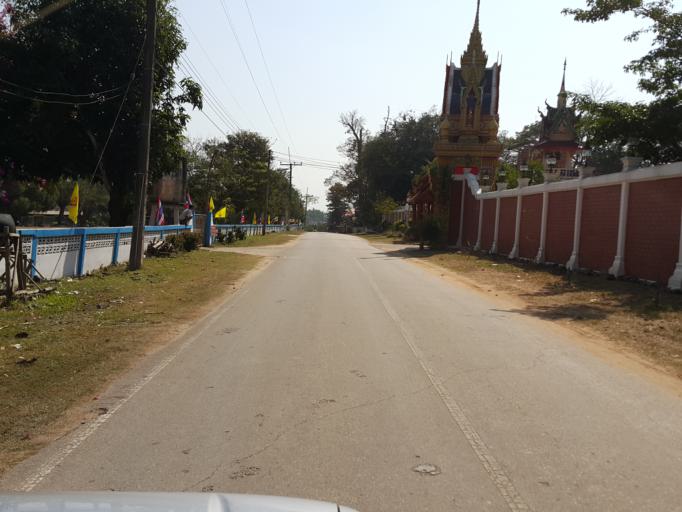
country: TH
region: Lampang
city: Wang Nuea
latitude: 19.0415
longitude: 99.6242
